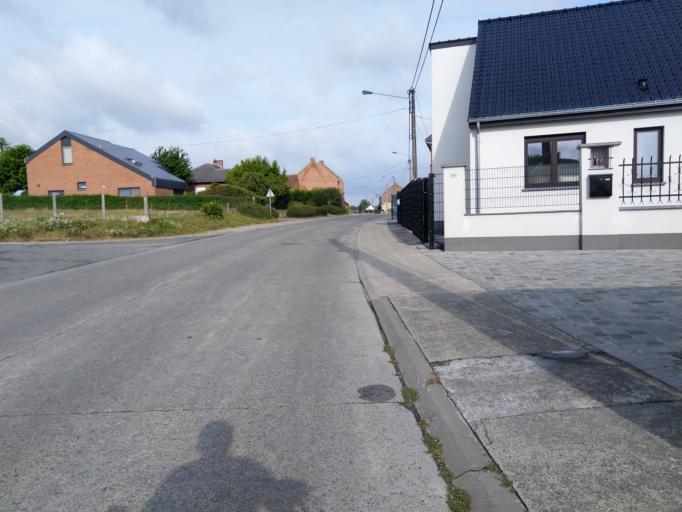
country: BE
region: Wallonia
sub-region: Province du Hainaut
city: Jurbise
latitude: 50.5291
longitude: 3.9028
